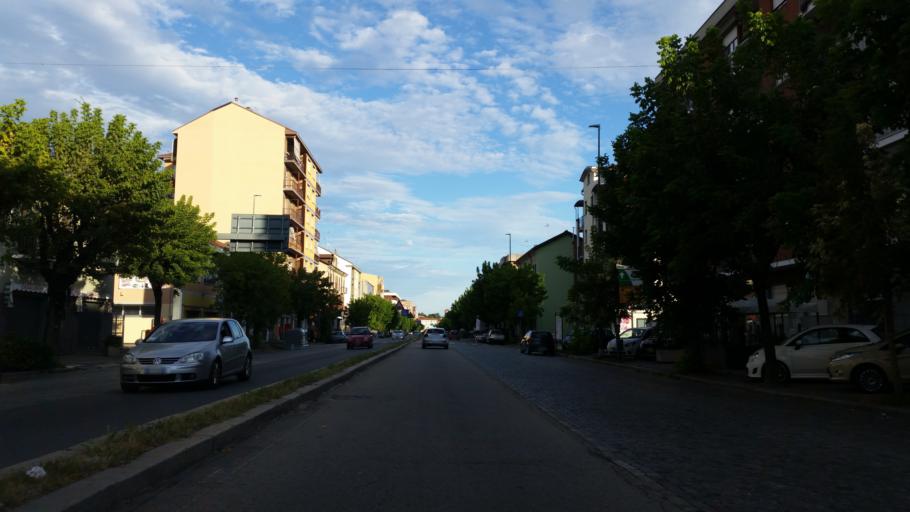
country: IT
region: Piedmont
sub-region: Provincia di Asti
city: Asti
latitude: 44.9055
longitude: 8.1863
